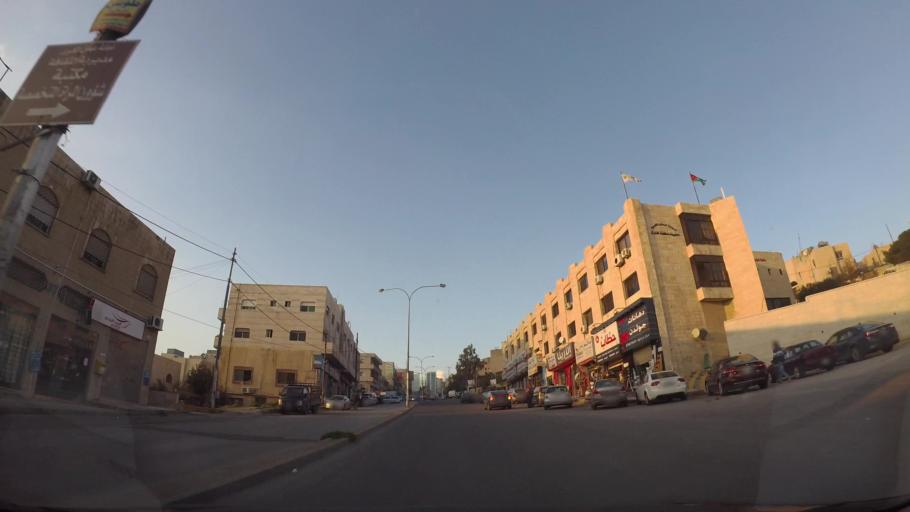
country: JO
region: Amman
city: Amman
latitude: 31.9947
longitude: 35.9459
